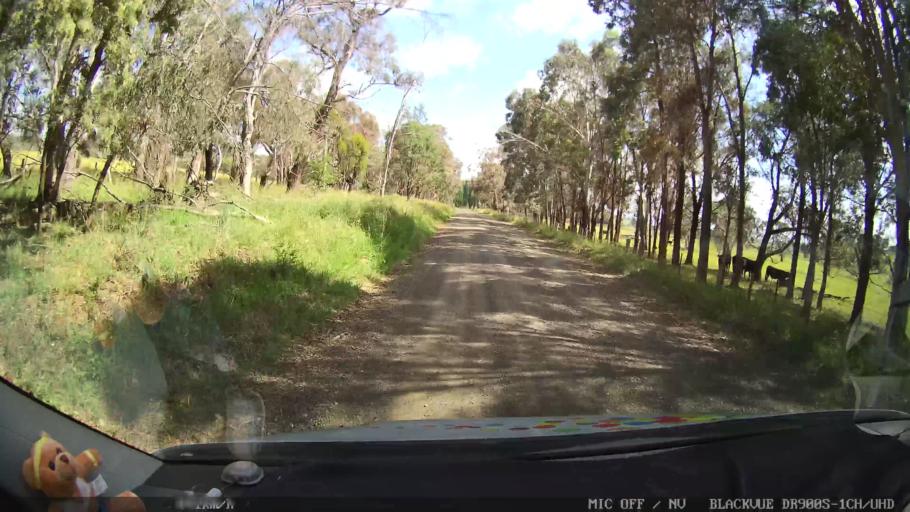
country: AU
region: New South Wales
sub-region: Glen Innes Severn
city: Glen Innes
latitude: -29.9666
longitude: 151.6993
